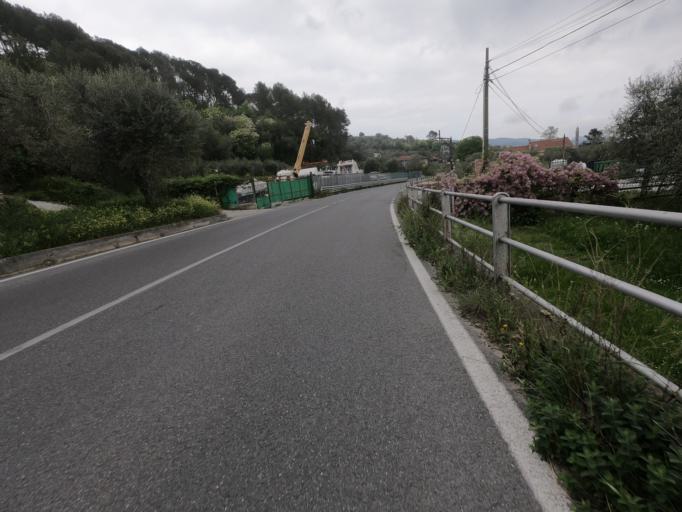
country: IT
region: Liguria
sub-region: Provincia di Savona
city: Villafranca
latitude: 44.0001
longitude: 8.1081
